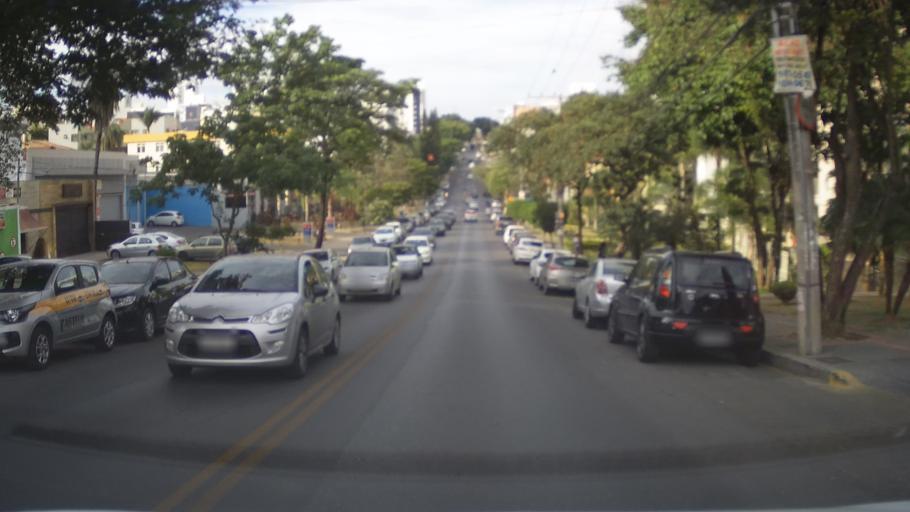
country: BR
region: Minas Gerais
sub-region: Belo Horizonte
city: Belo Horizonte
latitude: -19.8772
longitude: -43.9958
